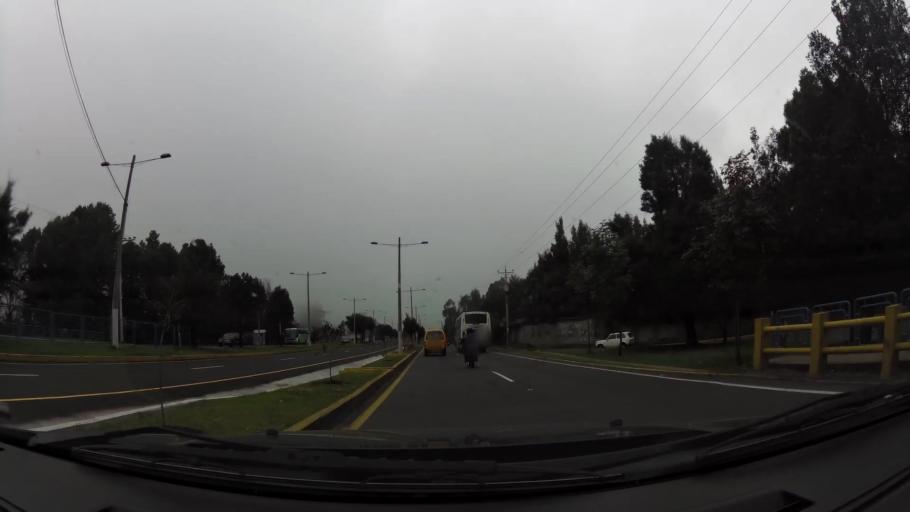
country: EC
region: Pichincha
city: Quito
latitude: -0.2640
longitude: -78.4880
